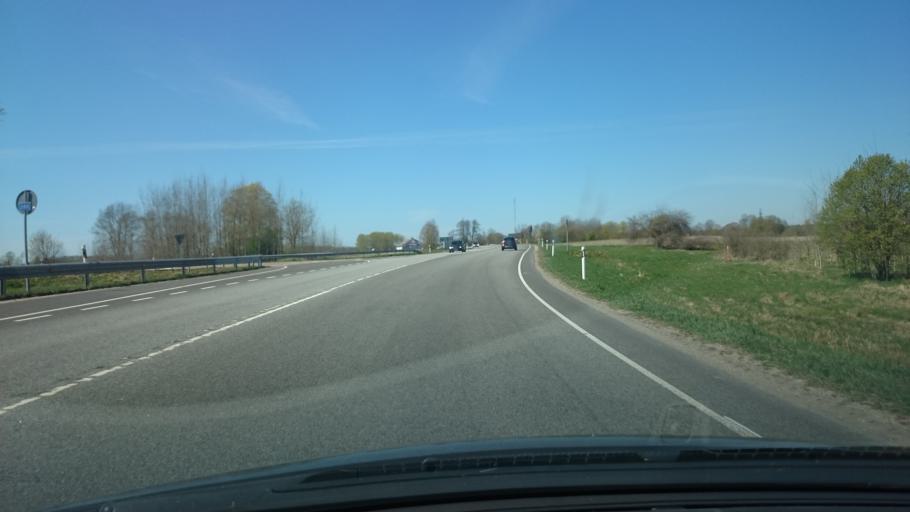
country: EE
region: Ida-Virumaa
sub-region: Narva-Joesuu linn
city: Narva-Joesuu
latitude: 59.3950
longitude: 28.0795
